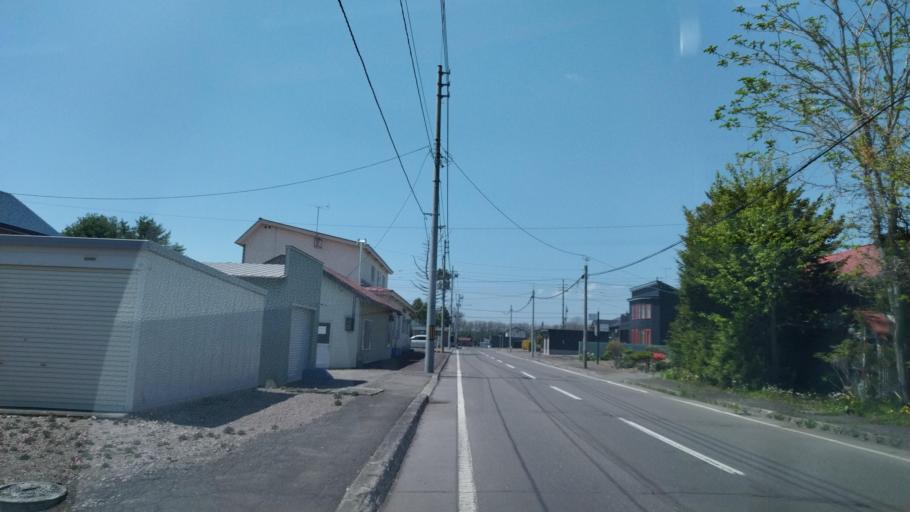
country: JP
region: Hokkaido
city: Otofuke
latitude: 43.1624
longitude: 143.2460
